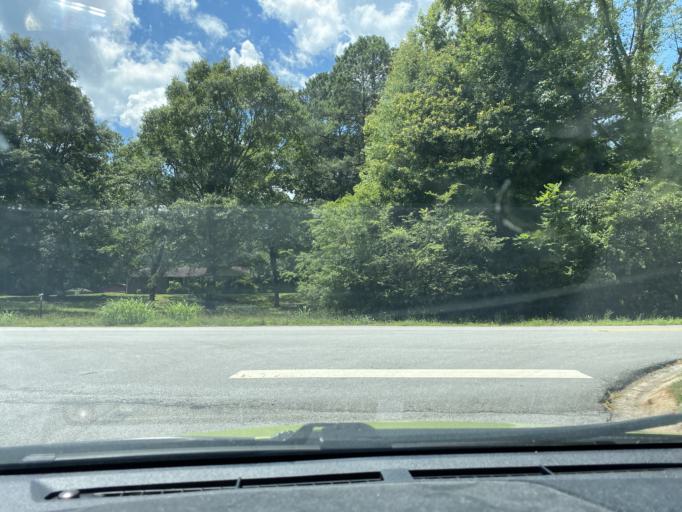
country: US
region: Georgia
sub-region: Fulton County
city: Palmetto
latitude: 33.4337
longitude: -84.6807
